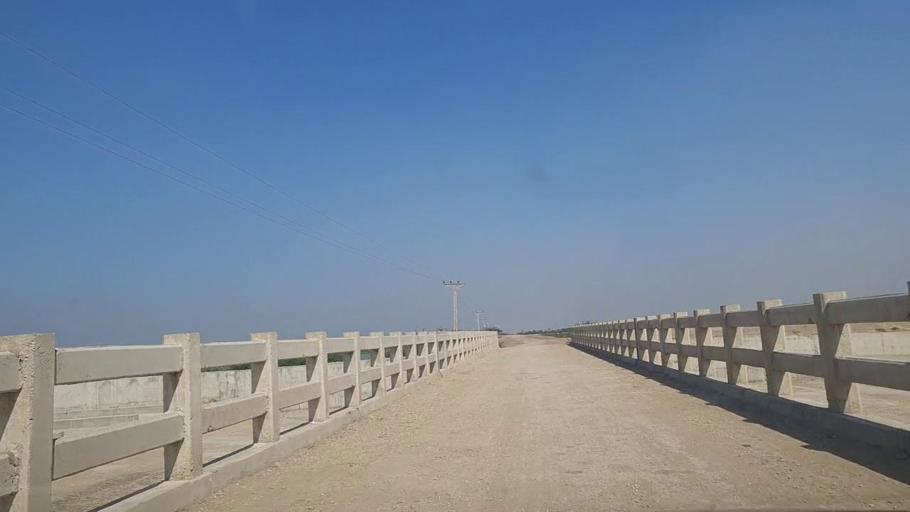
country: PK
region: Sindh
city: Daro Mehar
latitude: 24.9003
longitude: 68.0732
